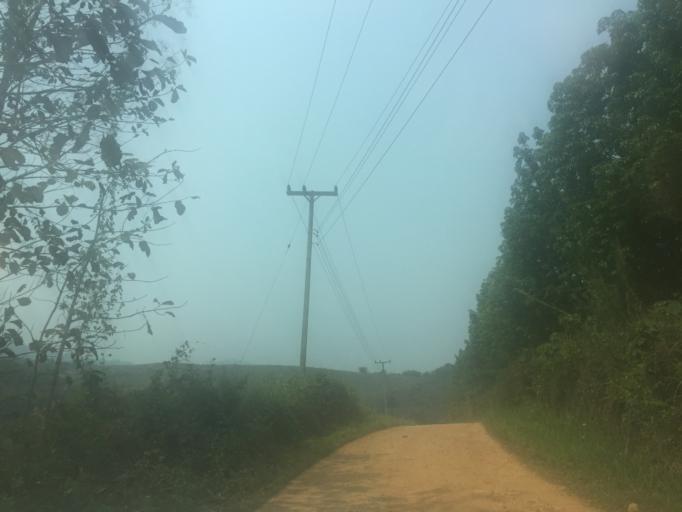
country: TH
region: Phayao
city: Phu Sang
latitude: 19.7714
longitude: 100.5352
